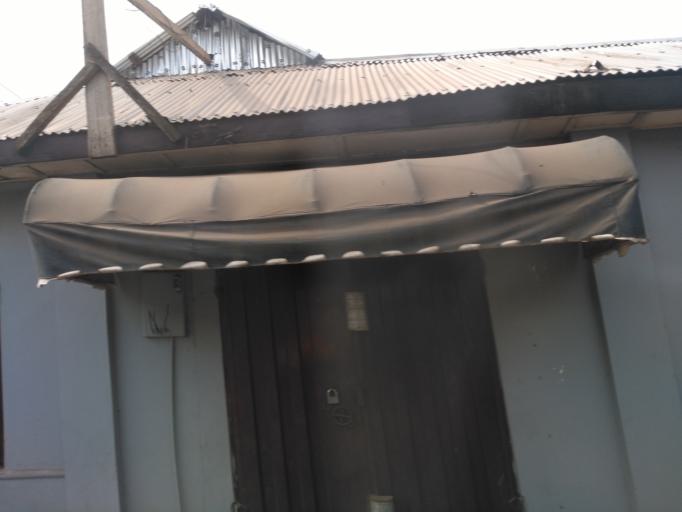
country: GH
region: Ashanti
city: Kumasi
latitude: 6.7046
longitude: -1.6200
